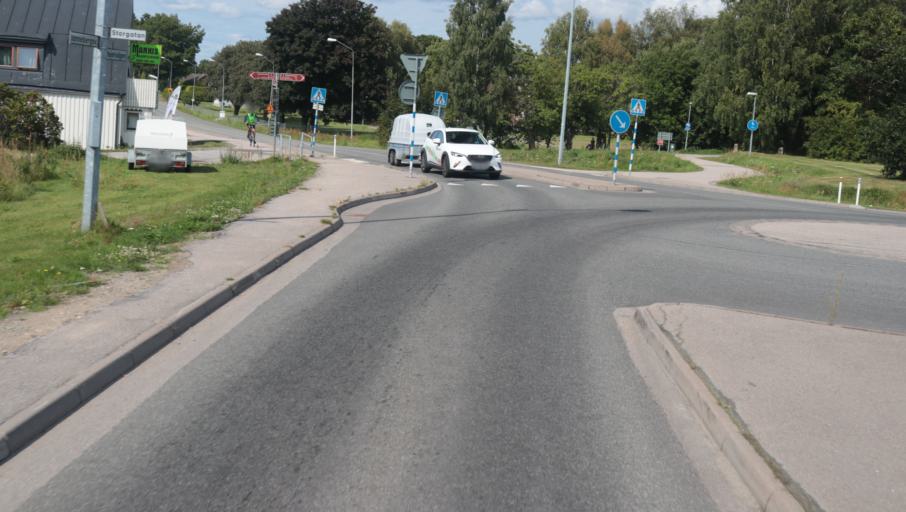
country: SE
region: Blekinge
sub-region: Karlshamns Kommun
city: Karlshamn
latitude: 56.1993
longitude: 14.8362
